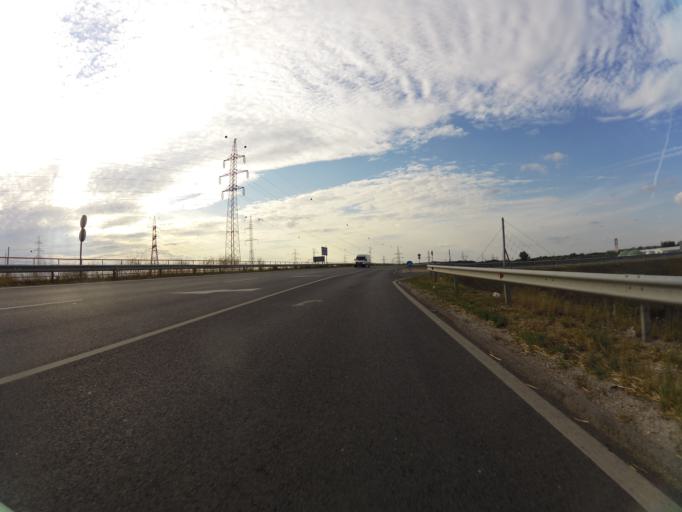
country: HU
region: Csongrad
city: Szeged
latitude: 46.2931
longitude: 20.1351
